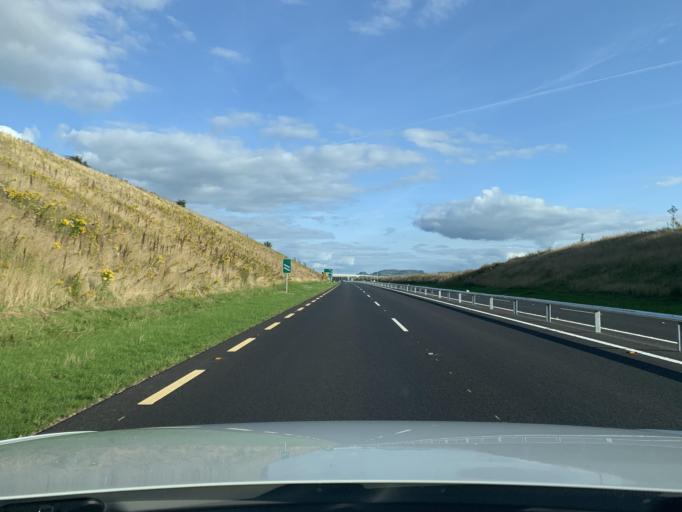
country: IE
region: Connaught
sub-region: Sligo
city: Collooney
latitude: 54.1279
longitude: -8.4482
